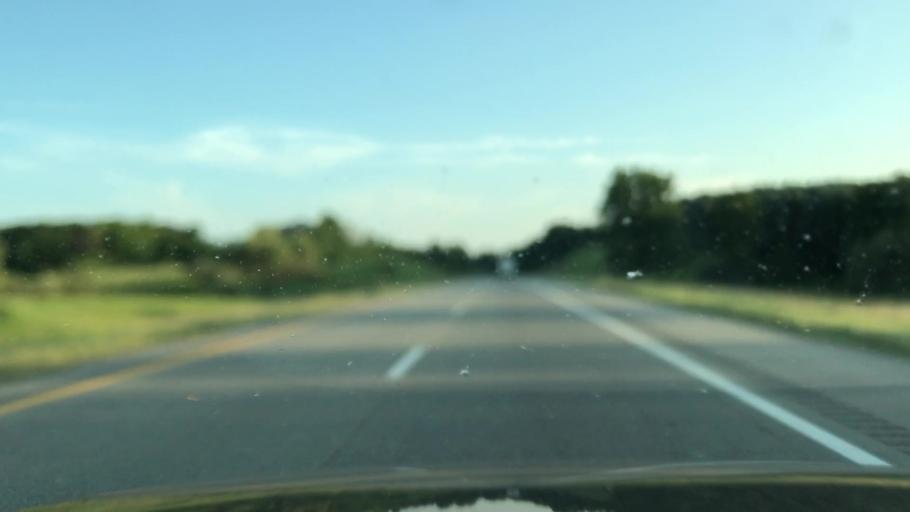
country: US
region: Michigan
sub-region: Osceola County
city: Reed City
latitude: 43.8713
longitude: -85.5319
